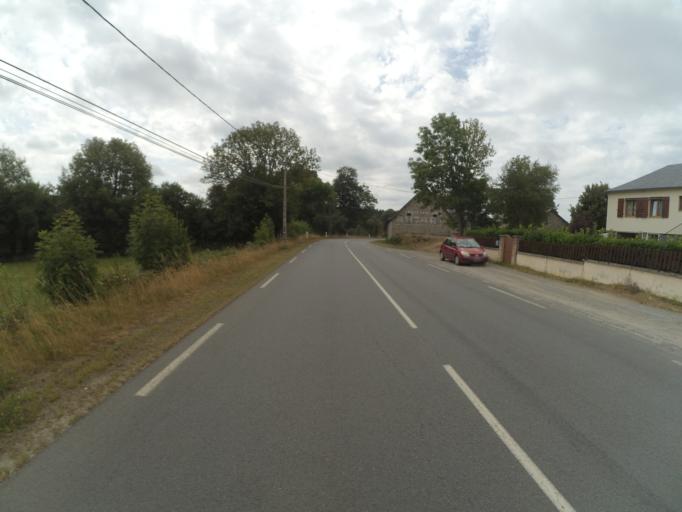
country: FR
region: Limousin
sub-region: Departement de la Correze
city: Ussel
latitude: 45.6008
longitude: 2.2925
